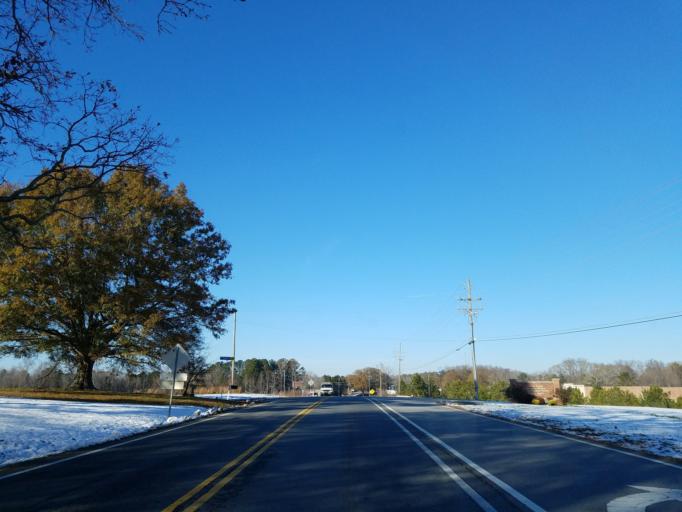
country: US
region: Georgia
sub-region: Dawson County
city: Dawsonville
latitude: 34.3558
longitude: -84.0321
